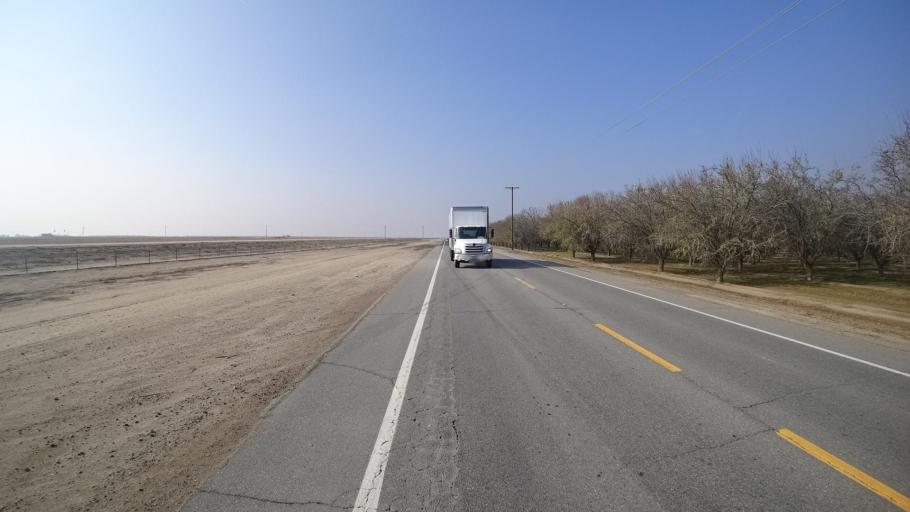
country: US
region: California
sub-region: Kern County
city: Rosedale
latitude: 35.3545
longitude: -119.2752
